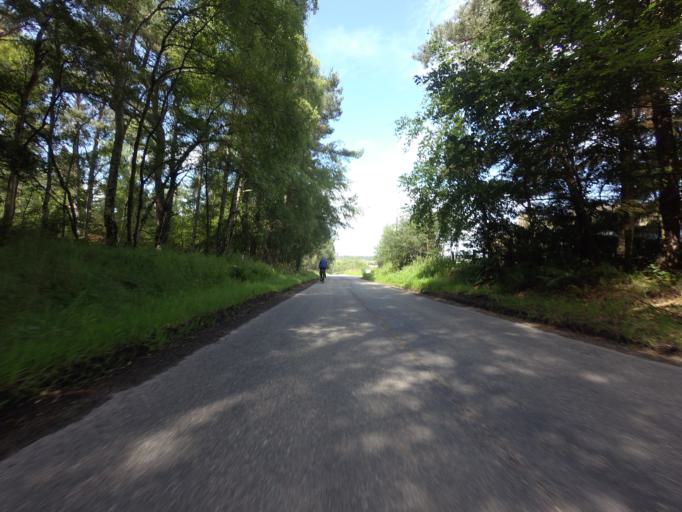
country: GB
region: Scotland
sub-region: Highland
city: Inverness
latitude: 57.5215
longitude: -4.2986
